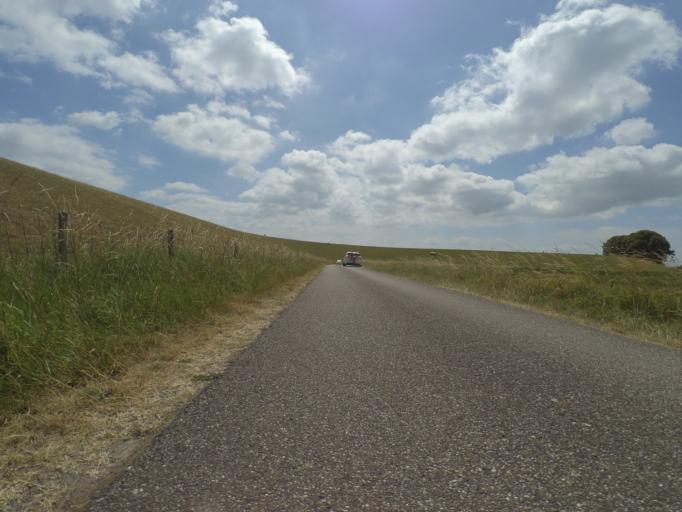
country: NL
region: Zeeland
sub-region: Gemeente Goes
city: Goes
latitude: 51.4267
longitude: 3.9183
